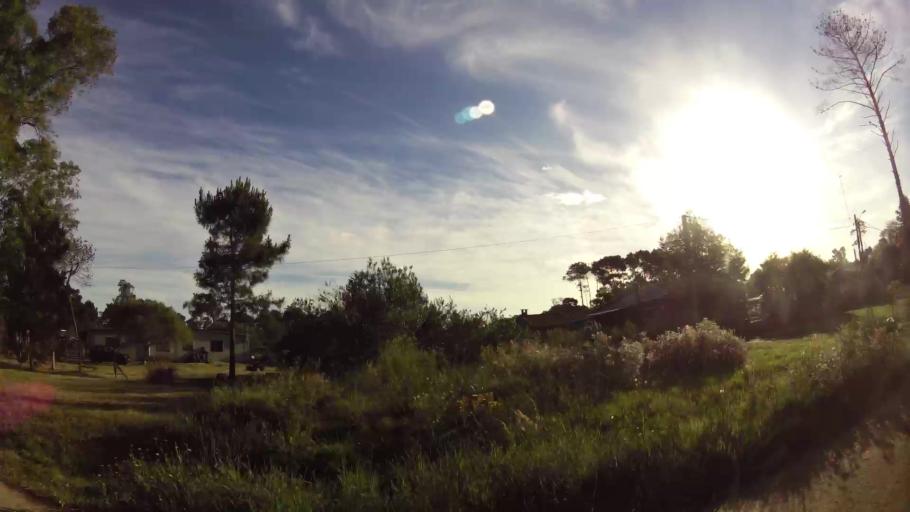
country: UY
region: Canelones
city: Empalme Olmos
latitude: -34.7698
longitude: -55.8582
